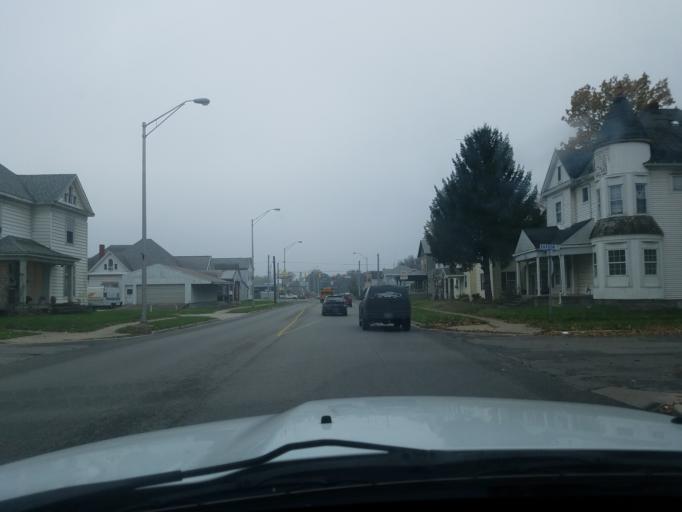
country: US
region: Indiana
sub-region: Cass County
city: Dunkirk
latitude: 40.7517
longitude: -86.3757
